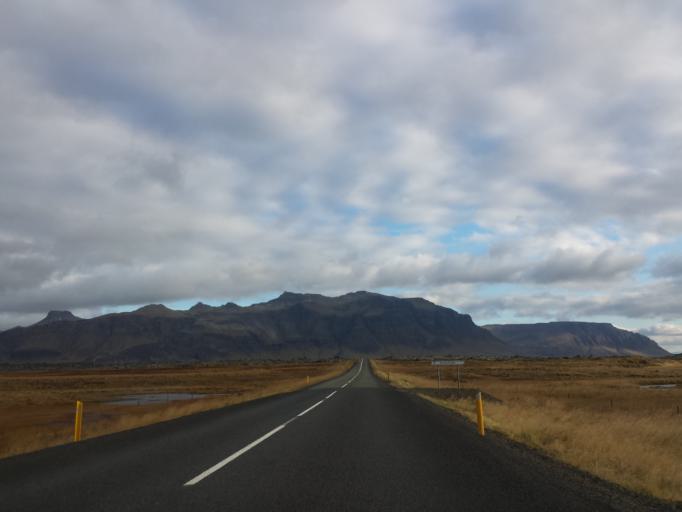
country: IS
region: West
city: Stykkisholmur
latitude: 64.8393
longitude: -22.3115
